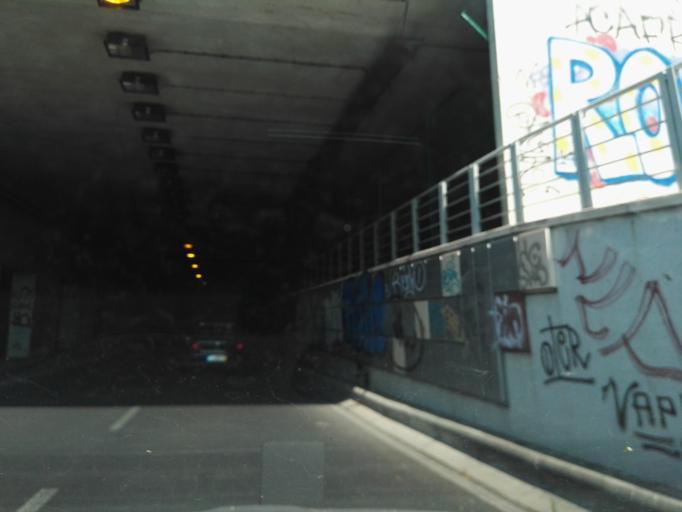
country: PT
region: Lisbon
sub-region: Lisbon
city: Lisbon
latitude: 38.7412
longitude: -9.1542
